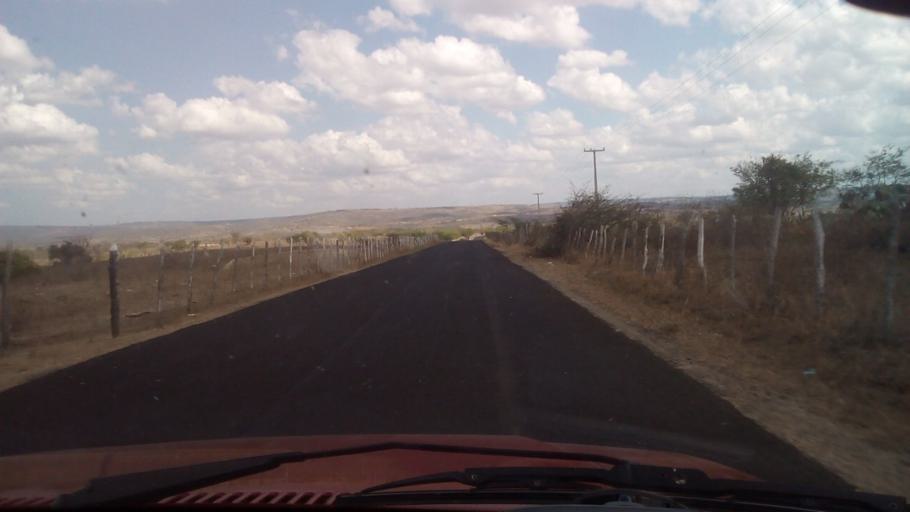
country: BR
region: Paraiba
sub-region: Cacimba De Dentro
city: Cacimba de Dentro
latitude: -6.6669
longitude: -35.7578
